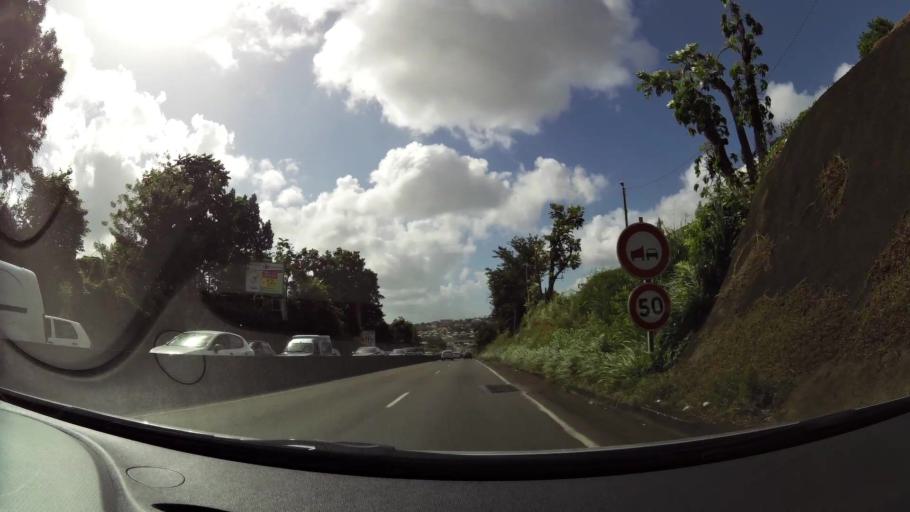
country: MQ
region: Martinique
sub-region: Martinique
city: Le Lamentin
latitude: 14.6191
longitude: -61.0000
